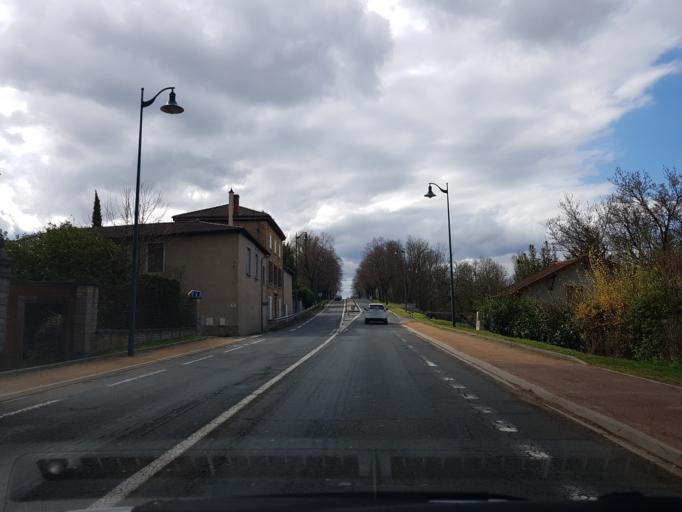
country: FR
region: Rhone-Alpes
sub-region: Departement du Rhone
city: Les Cheres
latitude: 45.8853
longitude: 4.7442
